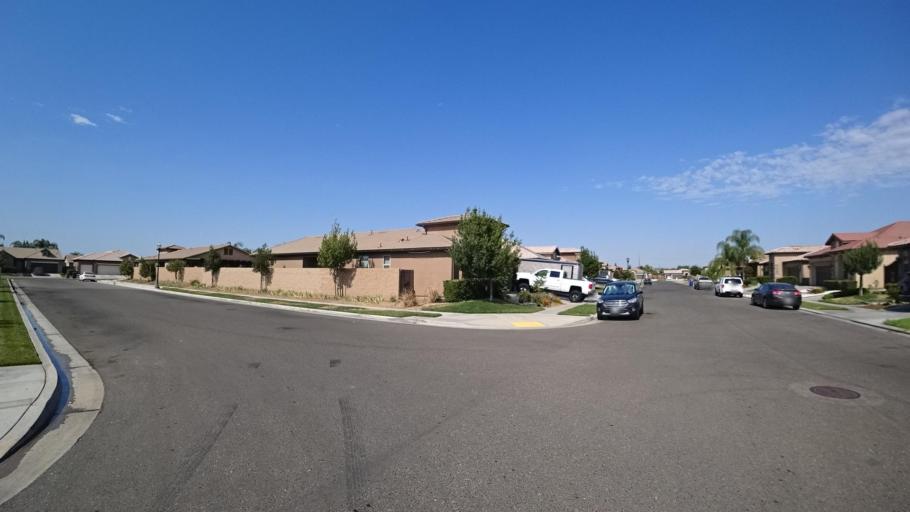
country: US
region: California
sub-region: Fresno County
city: Sunnyside
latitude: 36.7134
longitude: -119.6882
